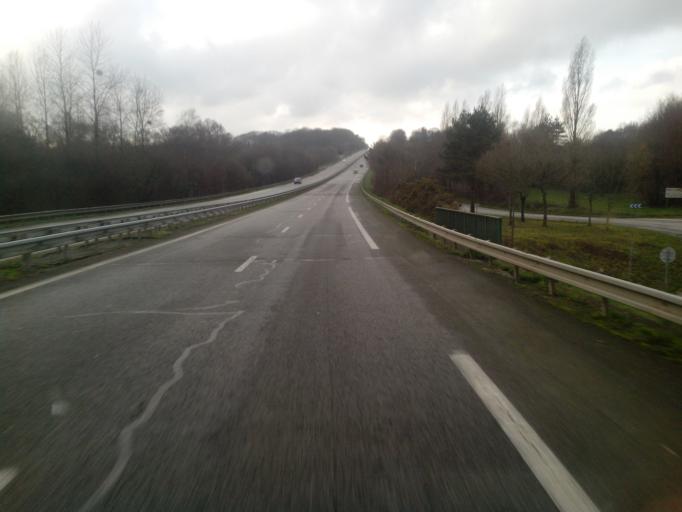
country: FR
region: Brittany
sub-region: Departement du Morbihan
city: Bignan
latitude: 47.9065
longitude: -2.7692
